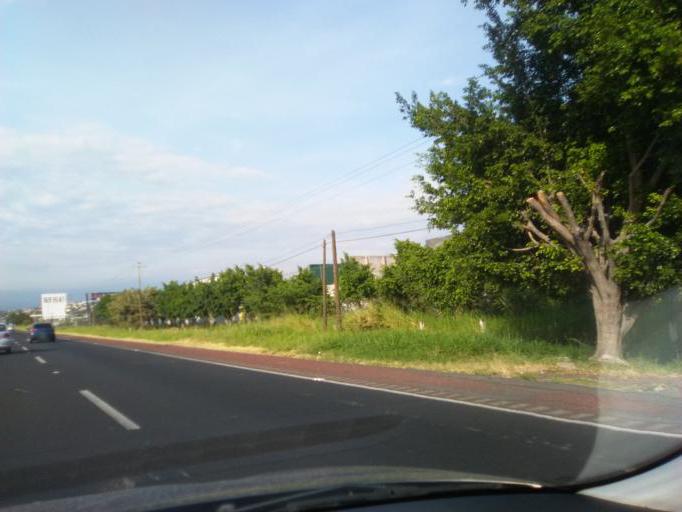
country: MX
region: Morelos
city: Temixco
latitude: 18.8239
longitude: -99.2184
